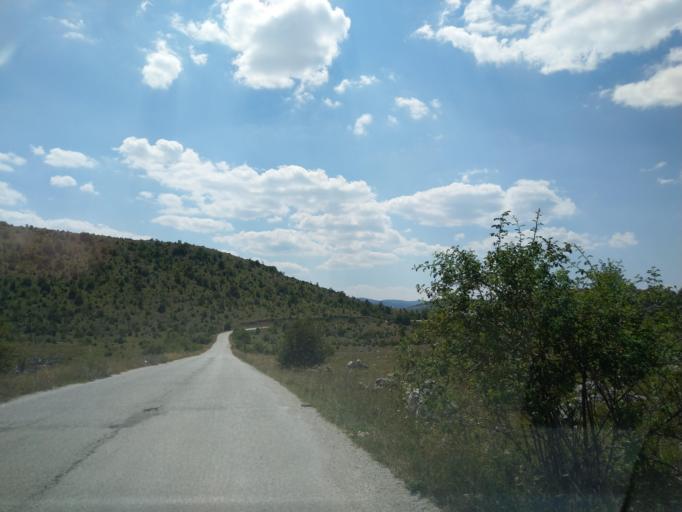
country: RS
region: Central Serbia
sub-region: Zlatiborski Okrug
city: Nova Varos
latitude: 43.4290
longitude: 19.9478
